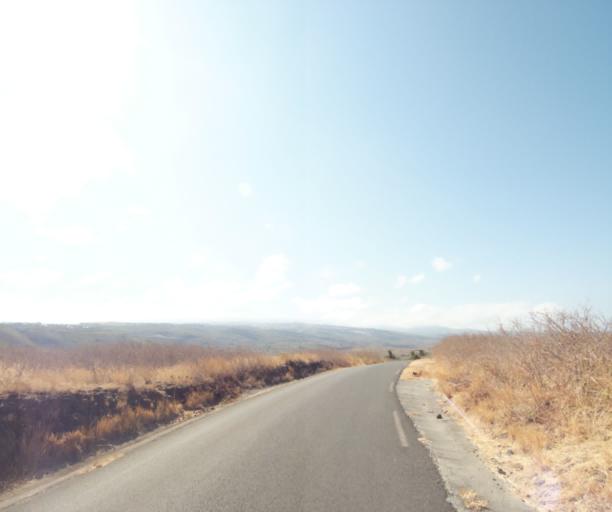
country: RE
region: Reunion
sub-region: Reunion
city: Trois-Bassins
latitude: -21.1022
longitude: 55.2508
